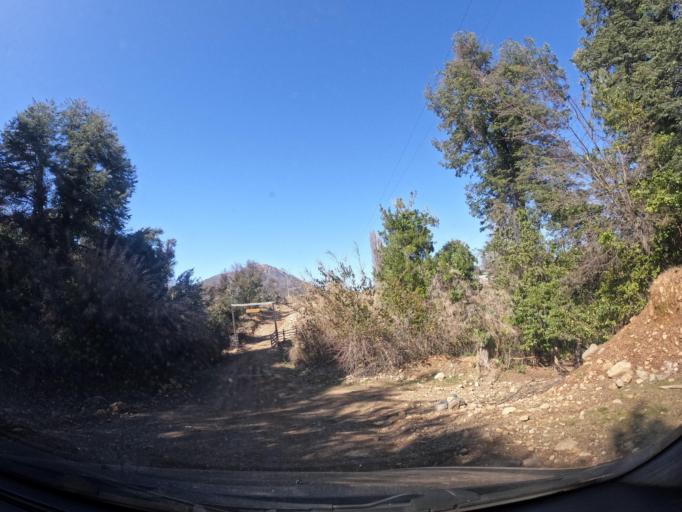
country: CL
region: Maule
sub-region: Provincia de Linares
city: Longavi
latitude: -36.2468
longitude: -71.3296
